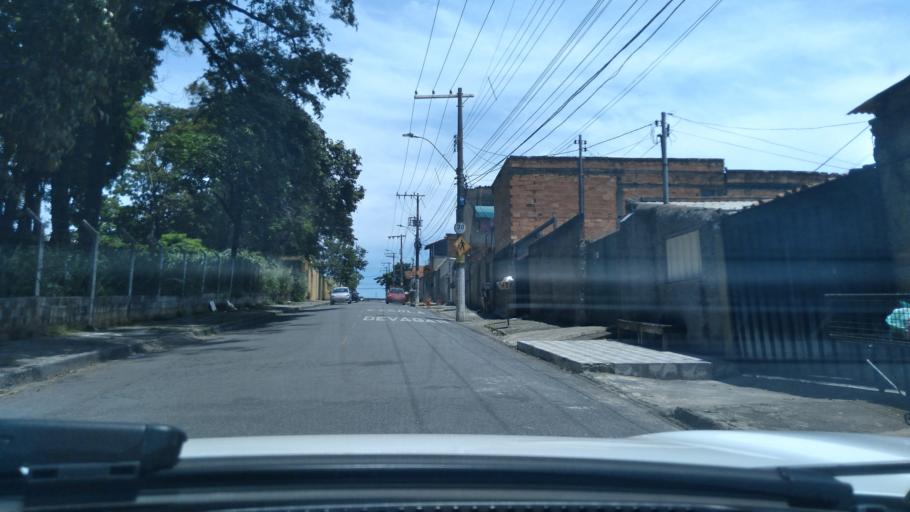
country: BR
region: Minas Gerais
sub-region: Contagem
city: Contagem
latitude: -19.9301
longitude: -44.0086
